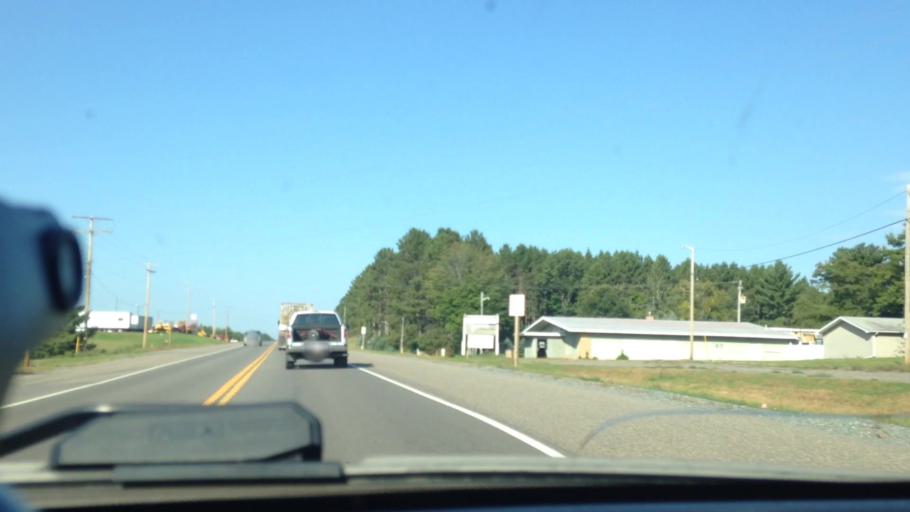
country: US
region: Michigan
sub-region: Dickinson County
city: Iron Mountain
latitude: 45.8761
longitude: -88.0896
